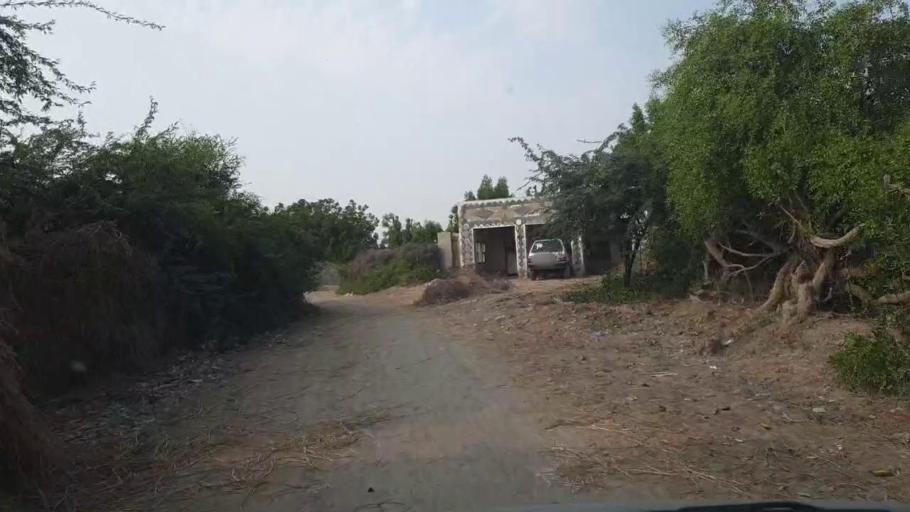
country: PK
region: Sindh
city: Matli
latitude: 25.0388
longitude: 68.7426
